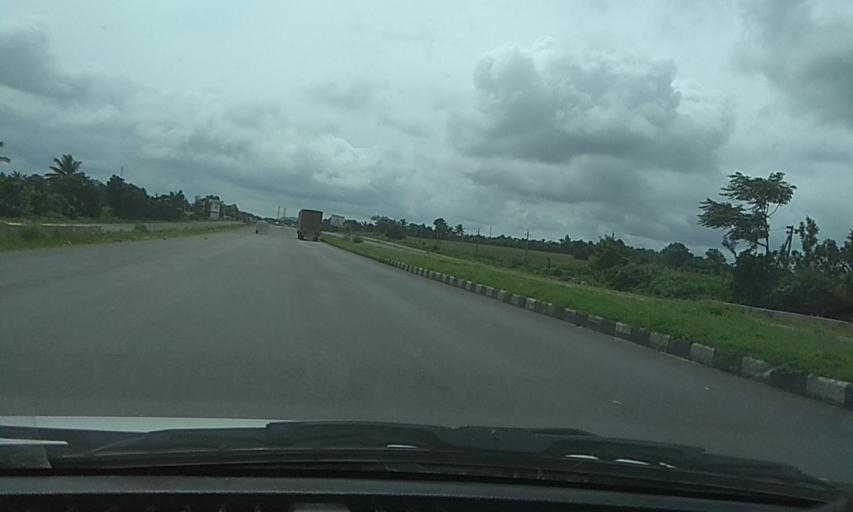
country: IN
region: Karnataka
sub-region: Davanagere
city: Mayakonda
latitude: 14.3818
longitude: 76.0869
